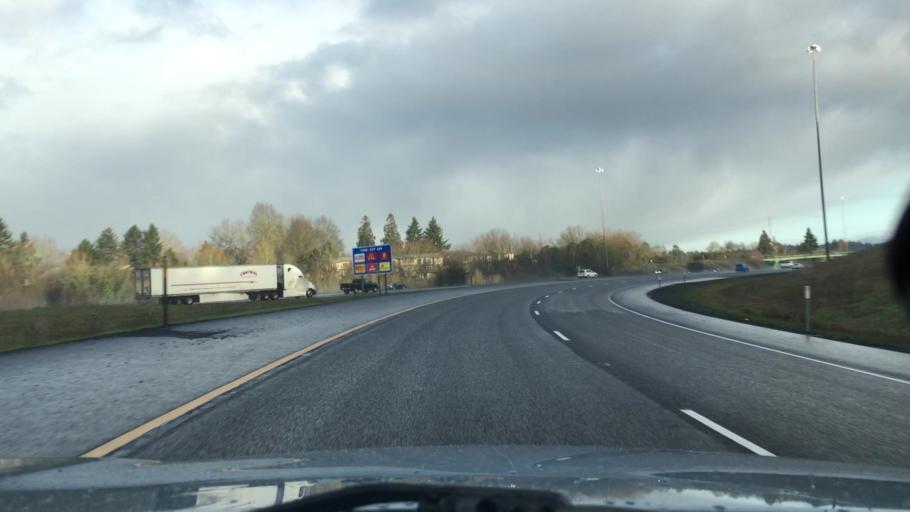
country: US
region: Oregon
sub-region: Washington County
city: Tualatin
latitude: 45.3720
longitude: -122.7557
